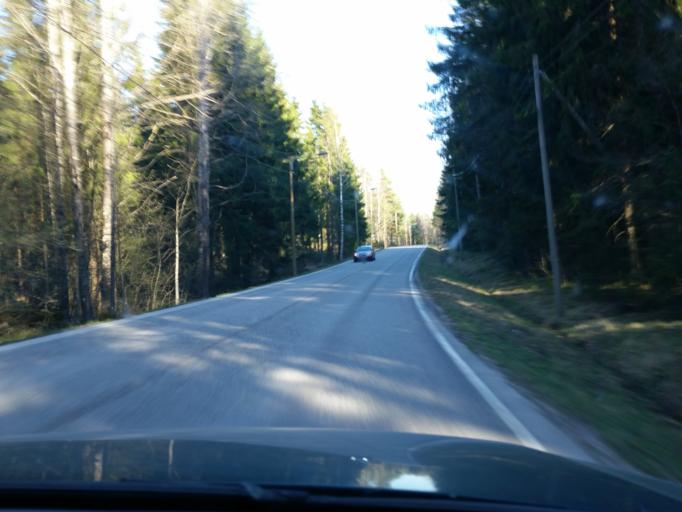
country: FI
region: Uusimaa
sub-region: Helsinki
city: Kirkkonummi
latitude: 60.1194
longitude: 24.5424
